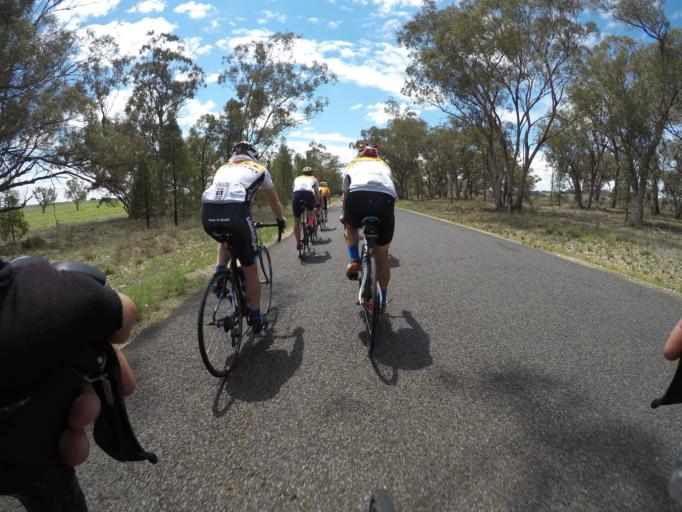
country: AU
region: New South Wales
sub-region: Dubbo Municipality
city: Dubbo
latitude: -32.3624
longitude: 148.5873
